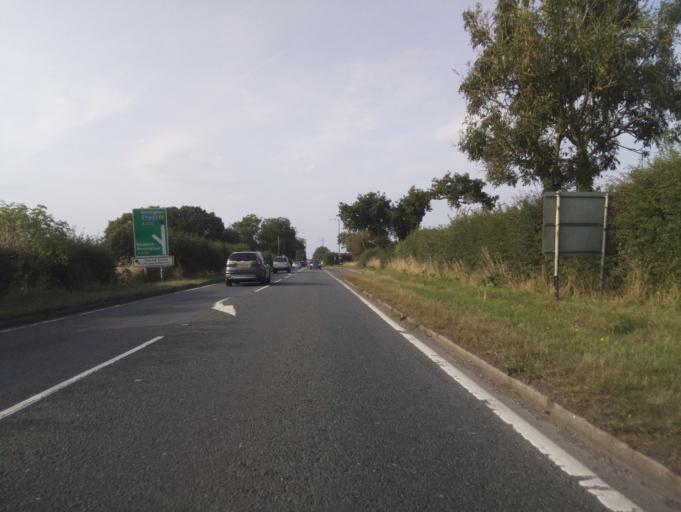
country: GB
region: England
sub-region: Warwickshire
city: Studley
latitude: 52.2576
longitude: -1.8892
